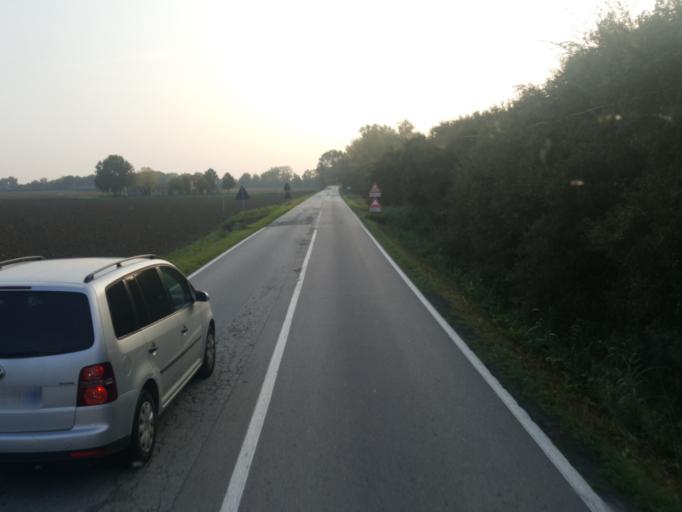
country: IT
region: Emilia-Romagna
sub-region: Provincia di Ravenna
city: Lavezzola
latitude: 44.5568
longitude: 11.8517
